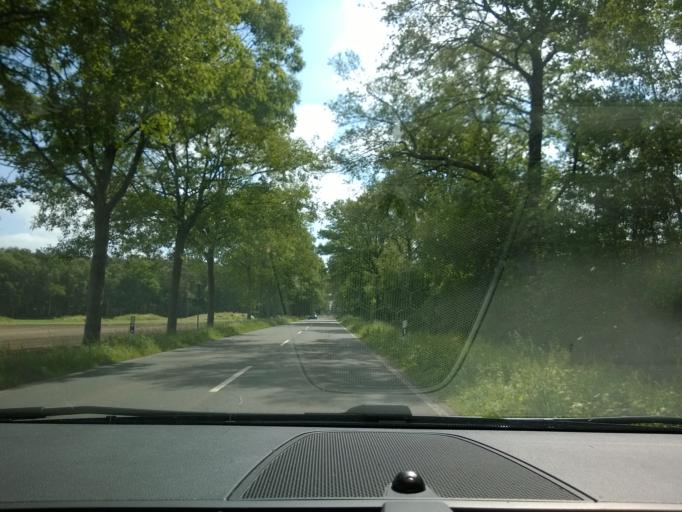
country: DE
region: North Rhine-Westphalia
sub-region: Regierungsbezirk Munster
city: Sudlohn
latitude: 51.9595
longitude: 6.8364
